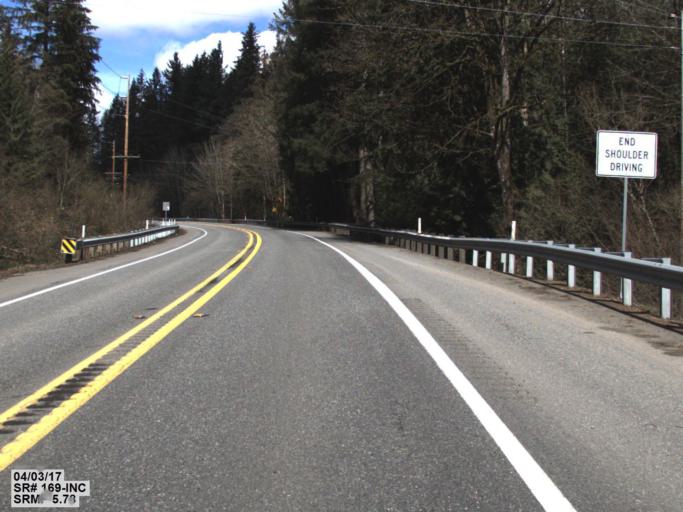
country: US
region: Washington
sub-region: King County
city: Black Diamond
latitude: 47.2845
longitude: -121.9892
